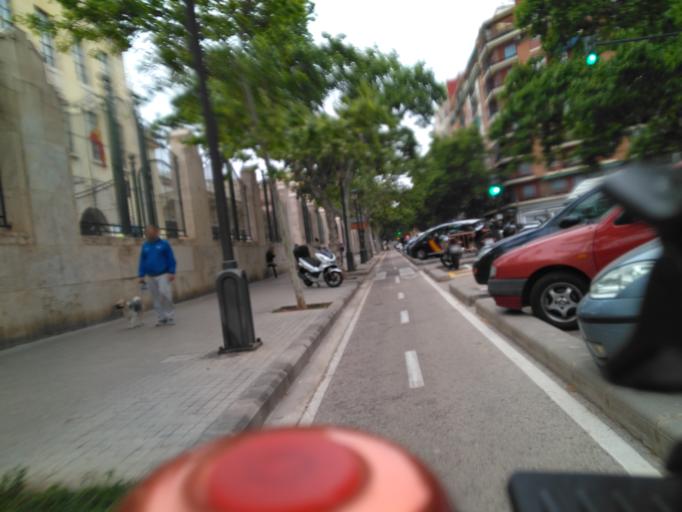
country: ES
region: Valencia
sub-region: Provincia de Valencia
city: Valencia
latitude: 39.4680
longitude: -0.3874
